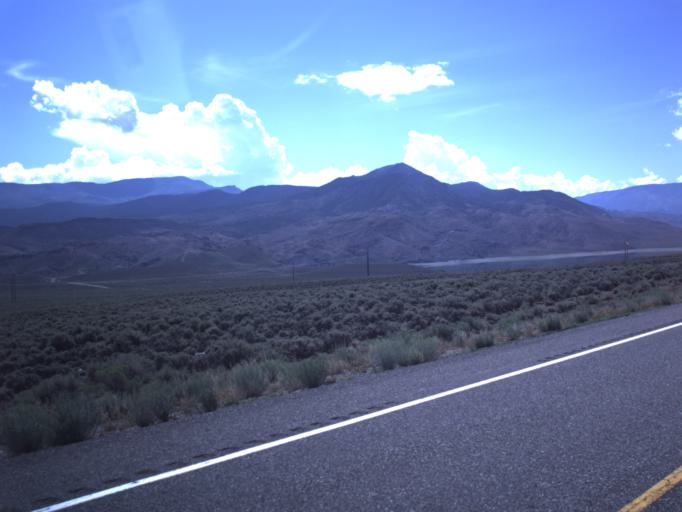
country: US
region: Utah
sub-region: Piute County
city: Junction
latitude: 38.3388
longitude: -112.2177
